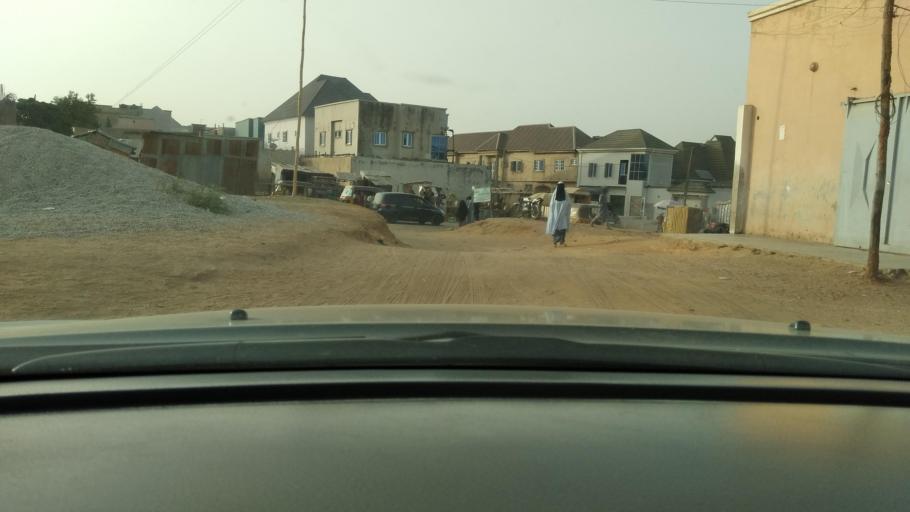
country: NG
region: Kano
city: Kano
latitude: 11.9499
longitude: 8.5199
